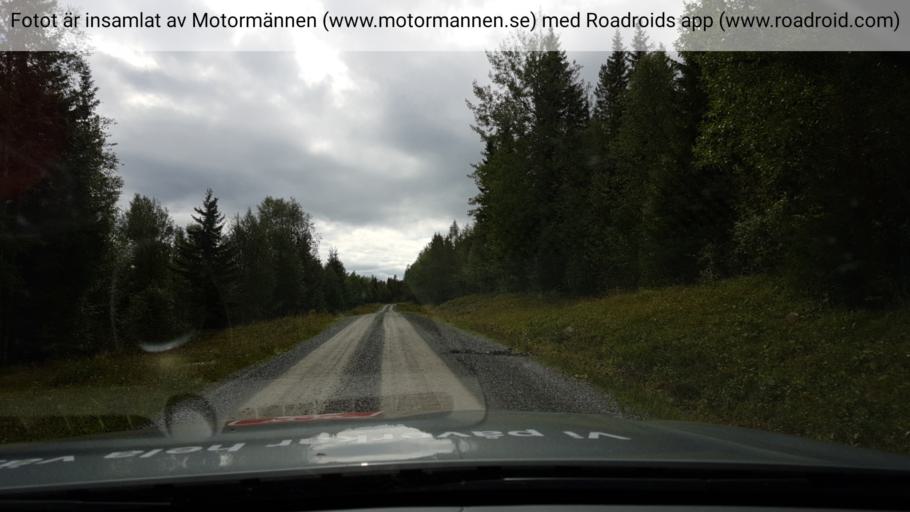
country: SE
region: Jaemtland
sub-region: Krokoms Kommun
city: Valla
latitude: 63.5252
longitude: 13.8983
